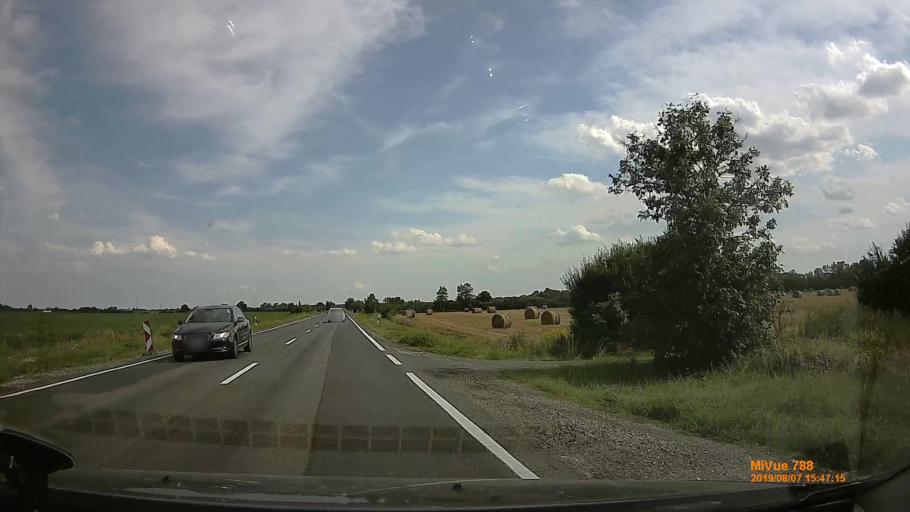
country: HU
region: Vas
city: Jak
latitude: 47.1738
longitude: 16.6256
